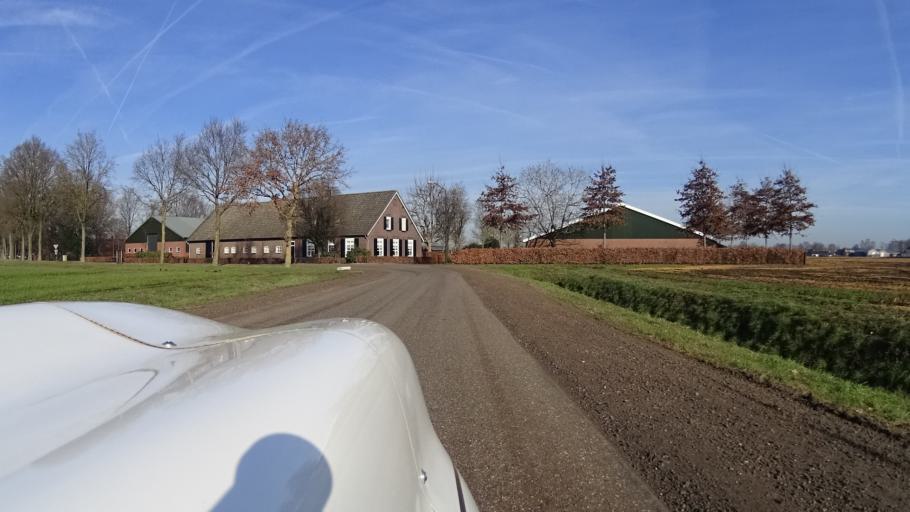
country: NL
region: North Brabant
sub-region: Gemeente Boekel
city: Boekel
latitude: 51.6010
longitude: 5.6598
